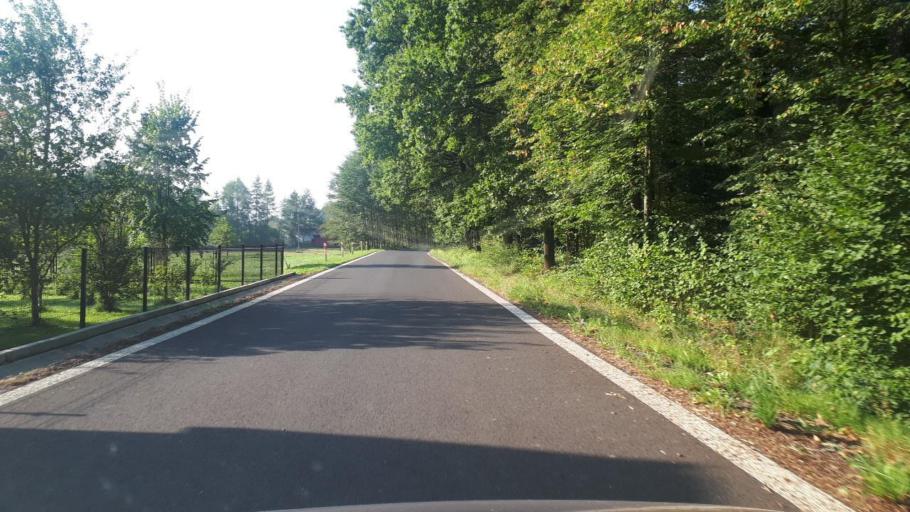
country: PL
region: Silesian Voivodeship
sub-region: Powiat cieszynski
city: Piersciec
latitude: 49.8535
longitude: 18.8399
